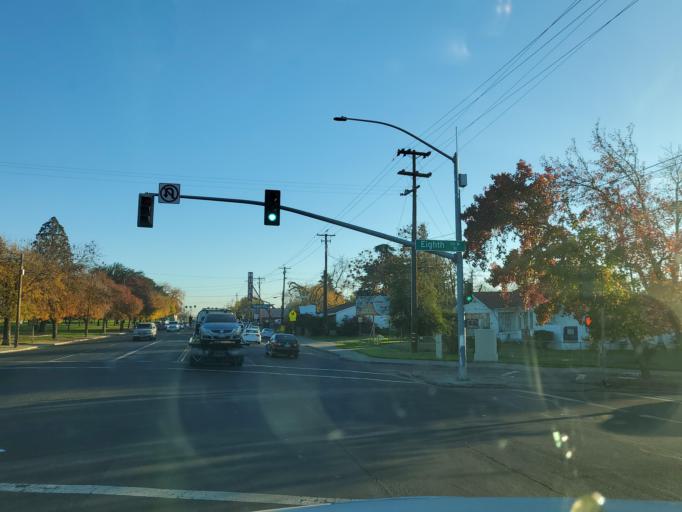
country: US
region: California
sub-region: San Joaquin County
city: Taft Mosswood
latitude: 37.9291
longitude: -121.2829
